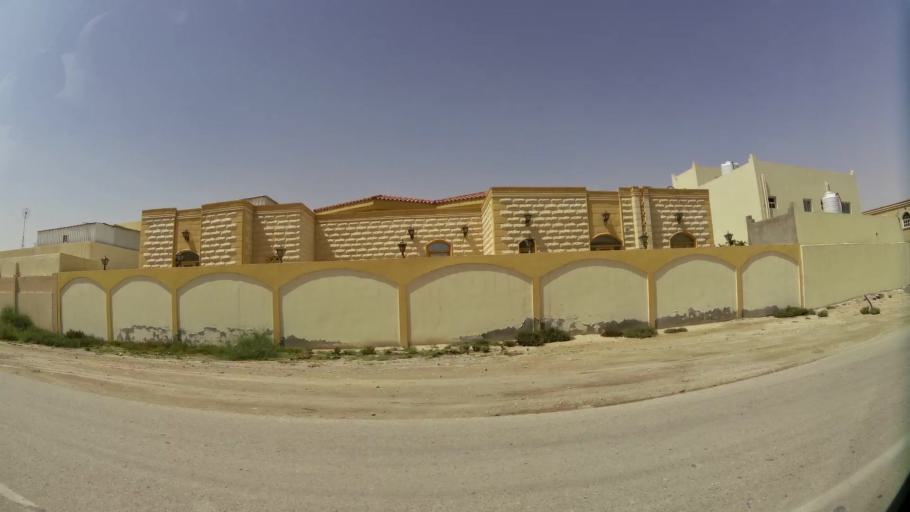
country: QA
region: Baladiyat Umm Salal
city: Umm Salal Muhammad
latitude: 25.3773
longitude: 51.4756
